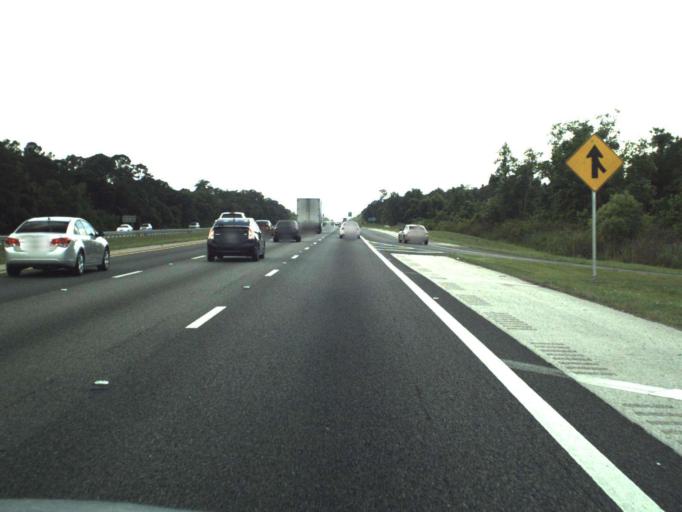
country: US
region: Florida
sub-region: Volusia County
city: Lake Helen
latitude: 28.9815
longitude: -81.2496
